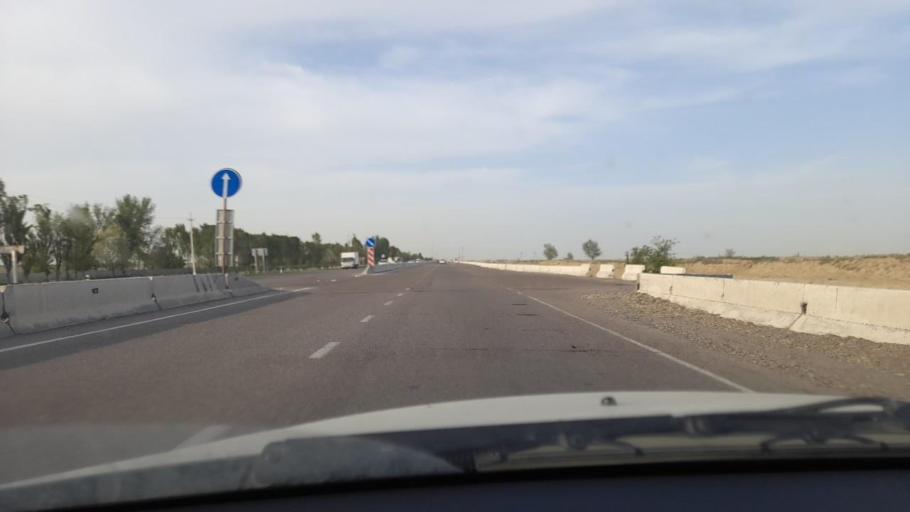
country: UZ
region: Jizzax
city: Dustlik
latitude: 40.4402
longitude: 68.2368
